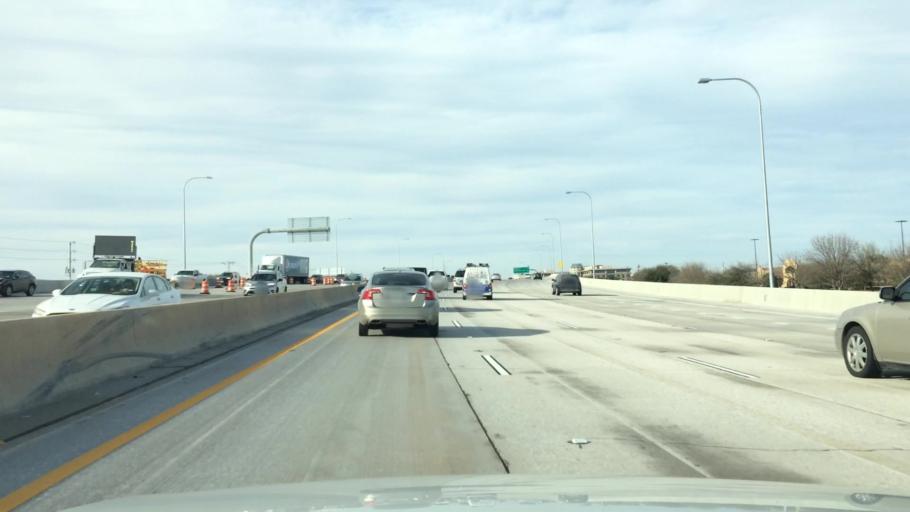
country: US
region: Texas
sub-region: Dallas County
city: Addison
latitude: 33.0246
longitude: -96.8298
